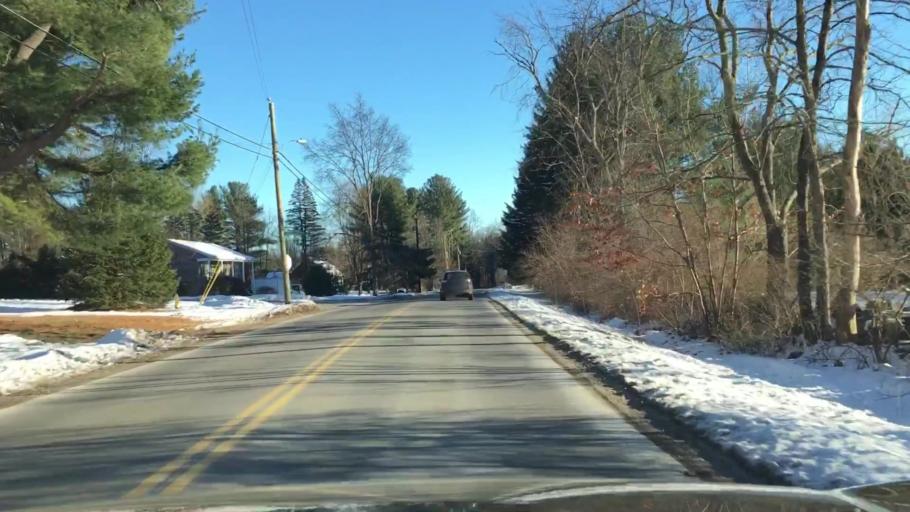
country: US
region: New Hampshire
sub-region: Hillsborough County
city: Milford
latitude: 42.8295
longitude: -71.5884
